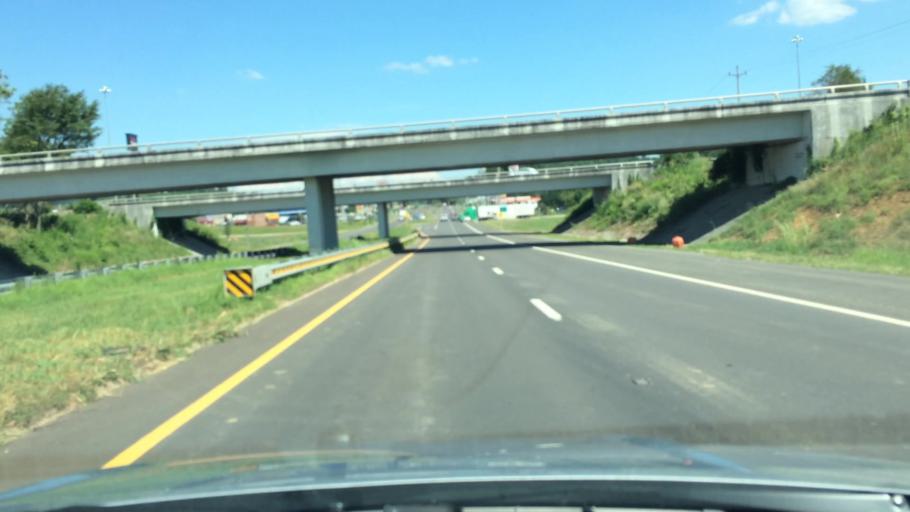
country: US
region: Tennessee
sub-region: McMinn County
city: Athens
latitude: 35.4664
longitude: -84.6496
